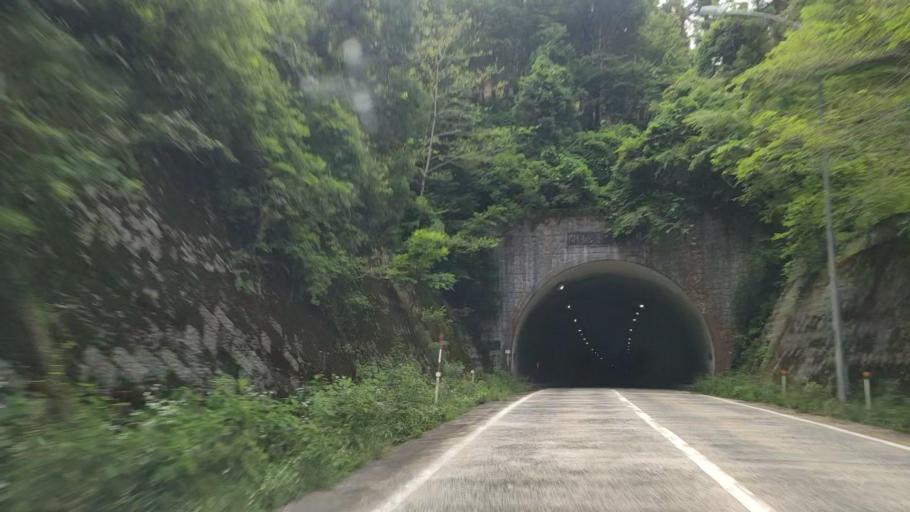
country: JP
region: Tottori
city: Yonago
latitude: 35.2699
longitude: 133.4348
